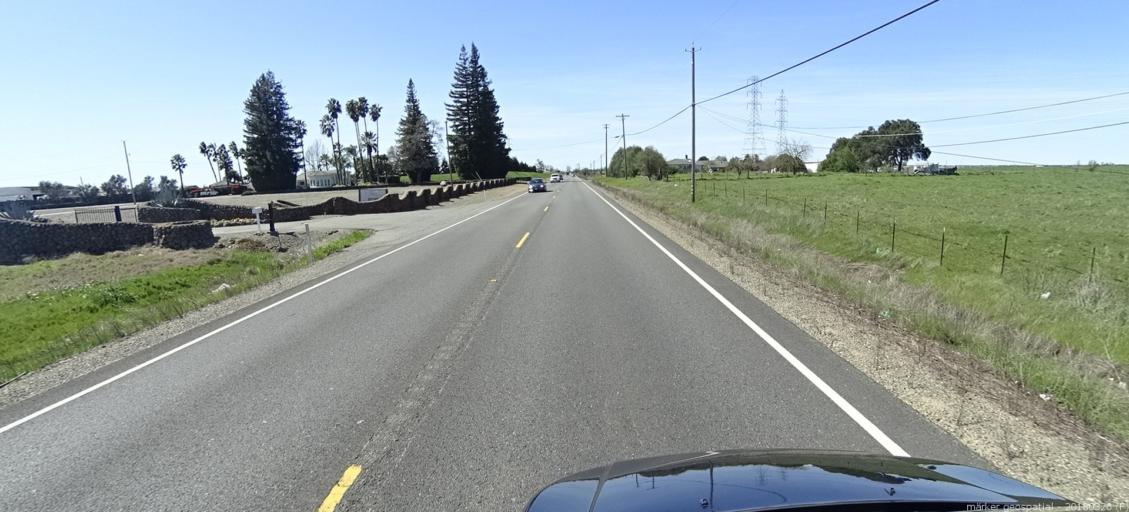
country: US
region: California
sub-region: Sacramento County
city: Rancho Cordova
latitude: 38.5150
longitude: -121.2834
